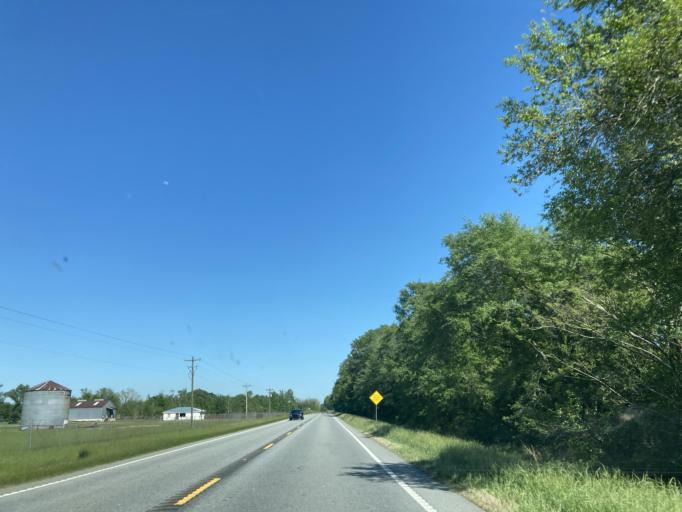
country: US
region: Georgia
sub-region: Miller County
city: Colquitt
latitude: 31.1837
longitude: -84.5556
